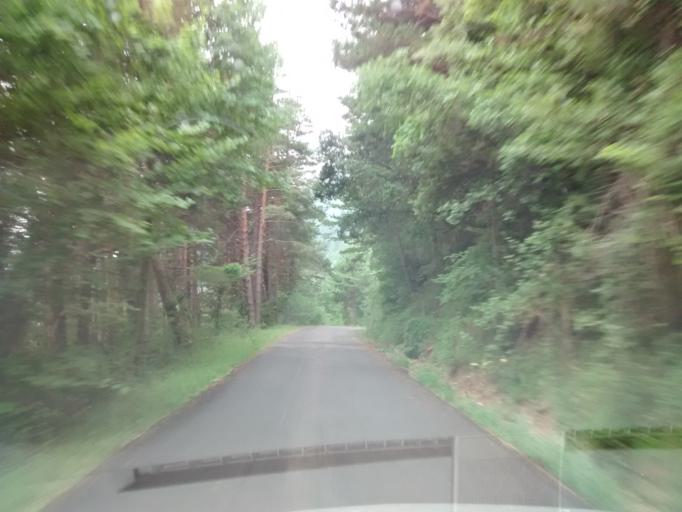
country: ES
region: Aragon
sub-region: Provincia de Huesca
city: Puertolas
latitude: 42.5760
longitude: 0.1402
